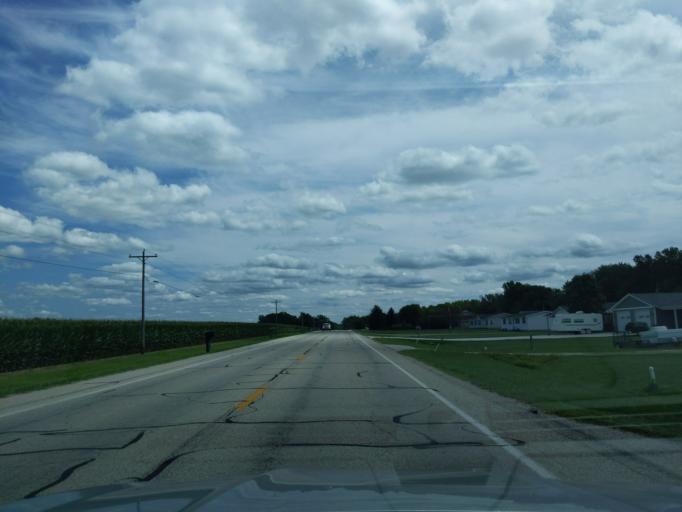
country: US
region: Indiana
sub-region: Ripley County
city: Batesville
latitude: 39.3084
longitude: -85.2669
